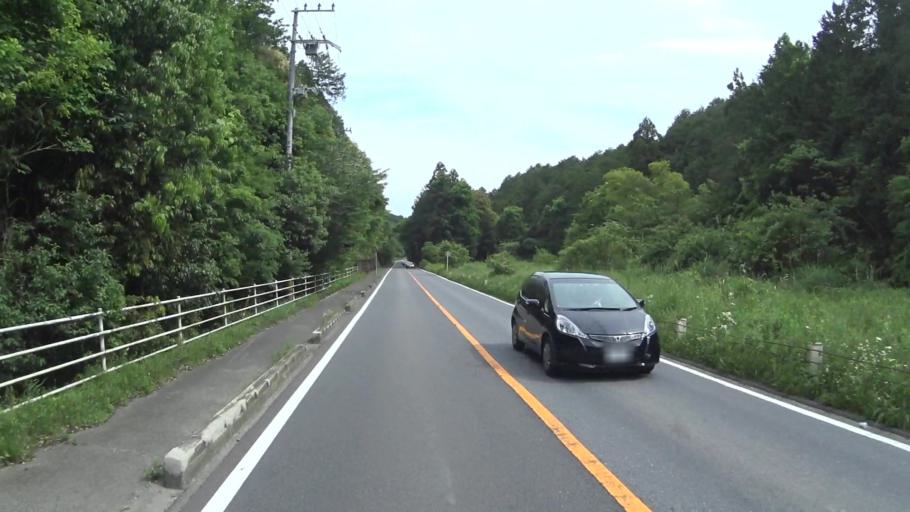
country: JP
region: Shiga Prefecture
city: Kitahama
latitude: 35.1464
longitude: 135.8786
